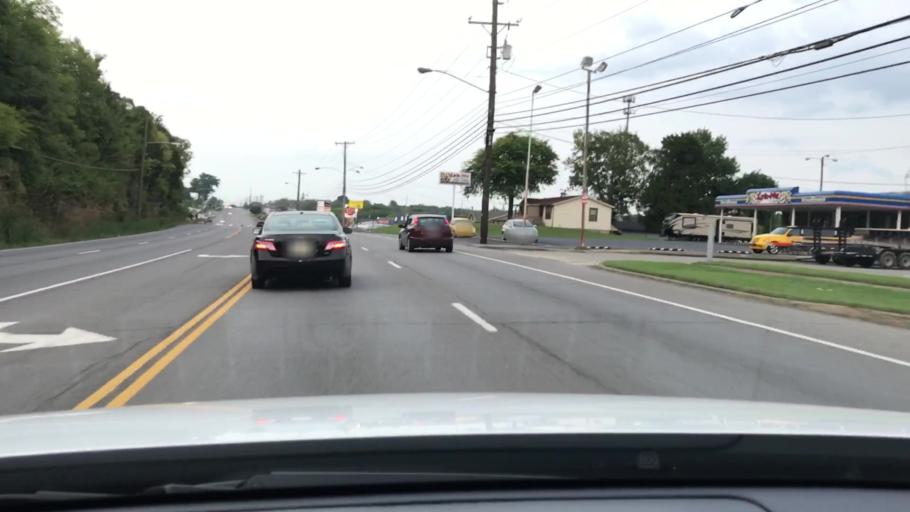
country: US
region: Tennessee
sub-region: Sumner County
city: Hendersonville
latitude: 36.3039
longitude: -86.6487
